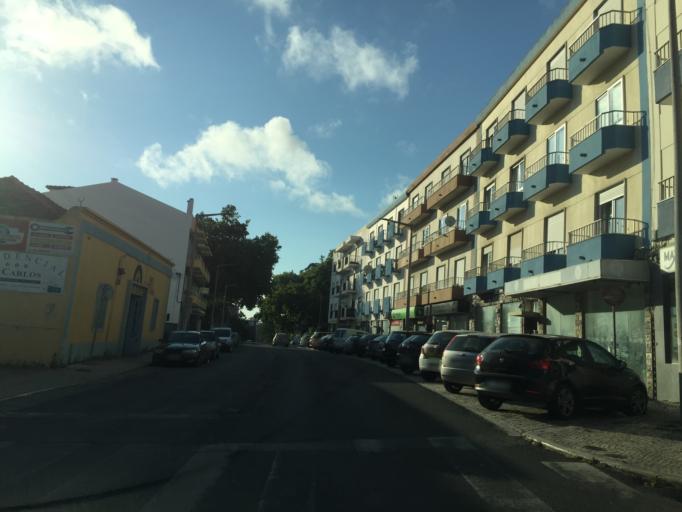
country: PT
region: Leiria
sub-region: Caldas da Rainha
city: Caldas da Rainha
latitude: 39.3989
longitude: -9.1341
